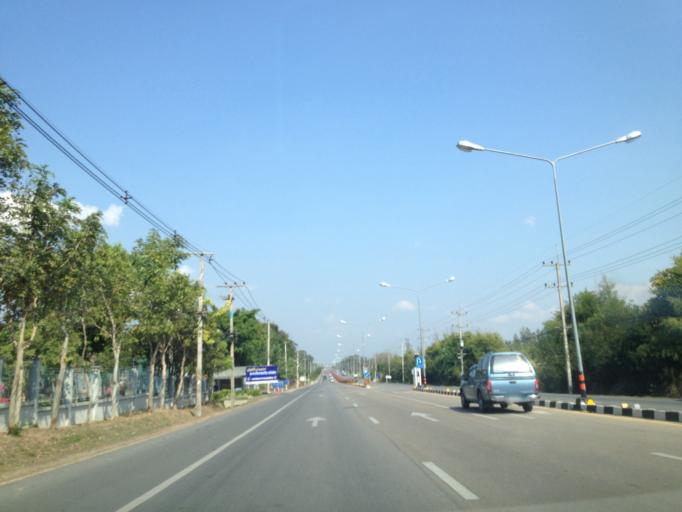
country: TH
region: Chiang Mai
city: Doi Lo
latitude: 18.4724
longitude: 98.7907
